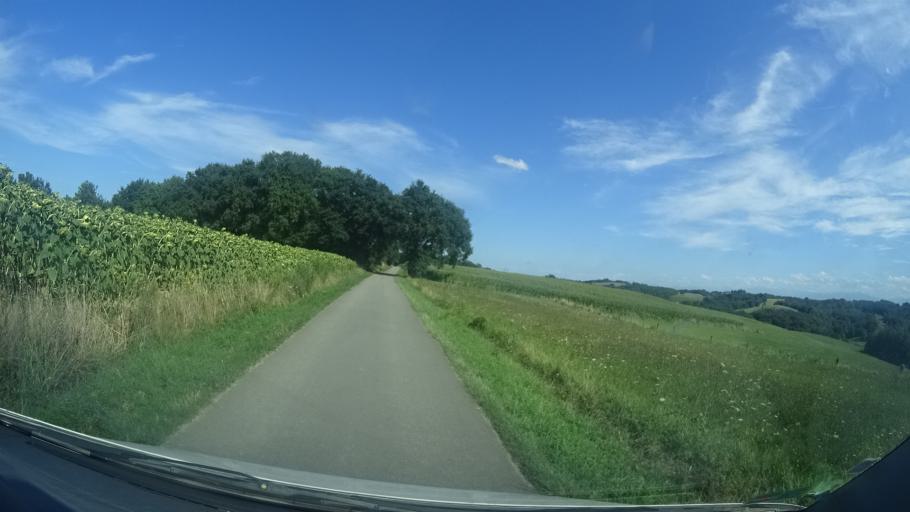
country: FR
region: Aquitaine
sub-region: Departement des Pyrenees-Atlantiques
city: Orthez
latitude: 43.5080
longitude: -0.6933
